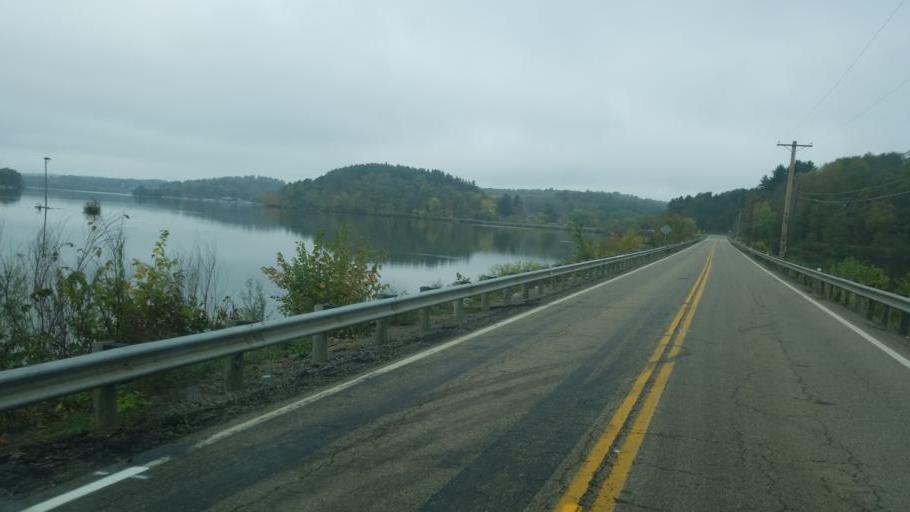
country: US
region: Ohio
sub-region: Carroll County
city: Lake Mohawk
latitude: 40.5586
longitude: -81.2017
